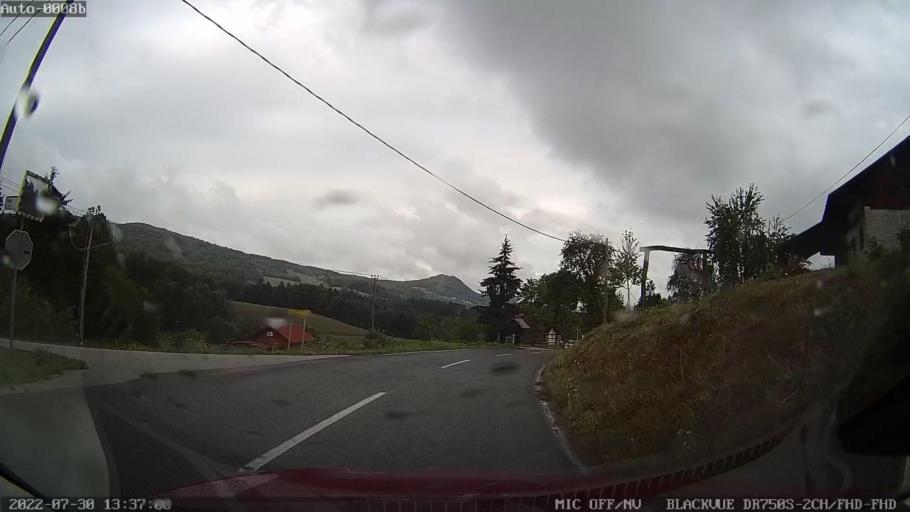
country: SI
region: Zuzemberk
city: Zuzemberk
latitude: 45.8744
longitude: 14.9190
